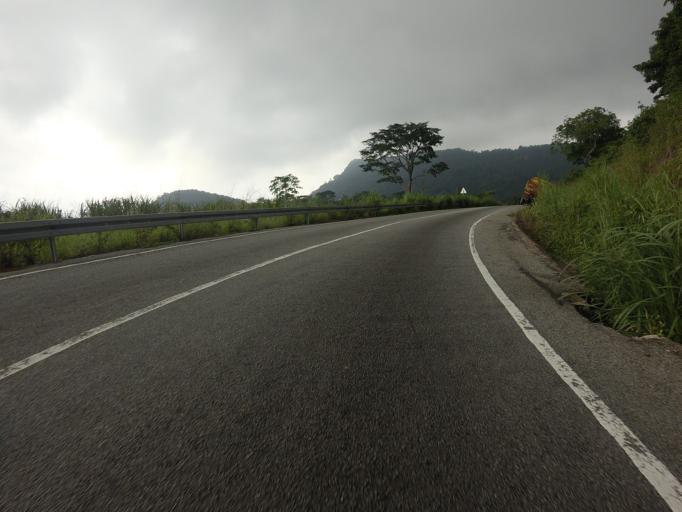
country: GH
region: Volta
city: Kpandu
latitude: 6.8167
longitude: 0.4224
